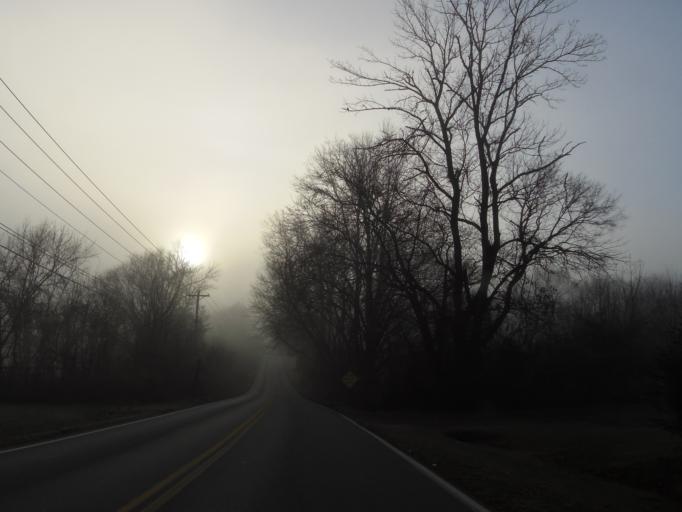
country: US
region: Tennessee
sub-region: Blount County
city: Eagleton Village
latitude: 35.8265
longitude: -83.9460
